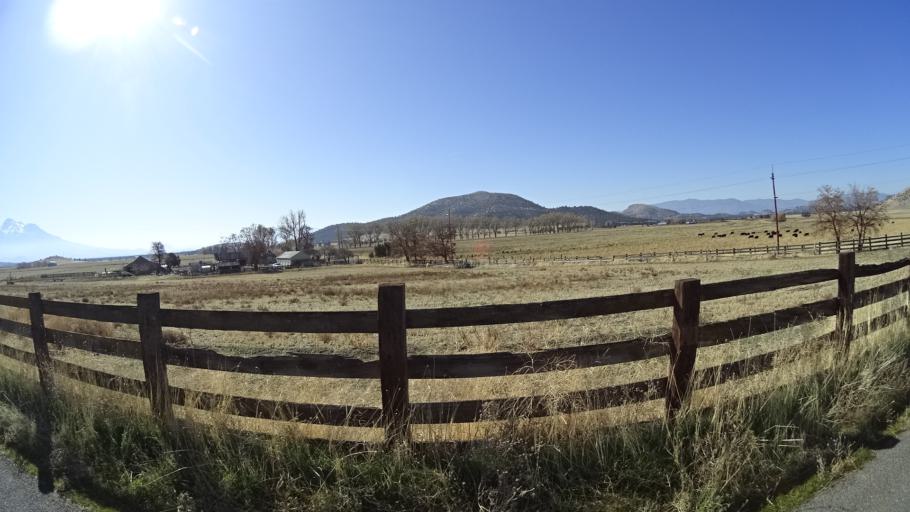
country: US
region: California
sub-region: Siskiyou County
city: Montague
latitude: 41.6883
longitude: -122.3689
